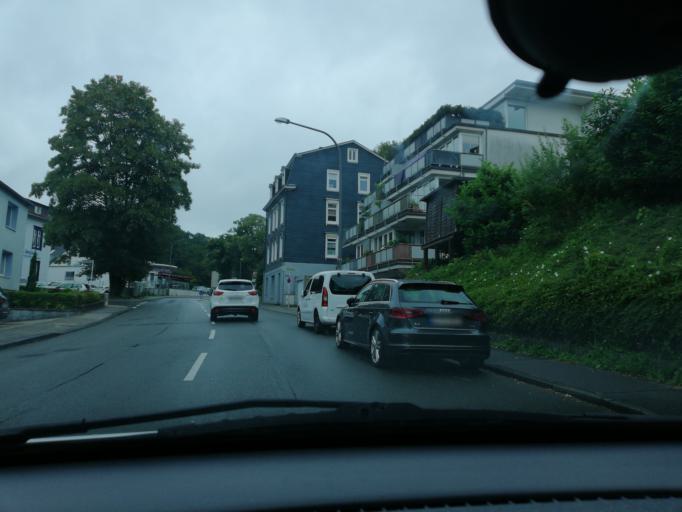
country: DE
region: North Rhine-Westphalia
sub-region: Regierungsbezirk Dusseldorf
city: Remscheid
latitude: 51.2300
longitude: 7.2074
